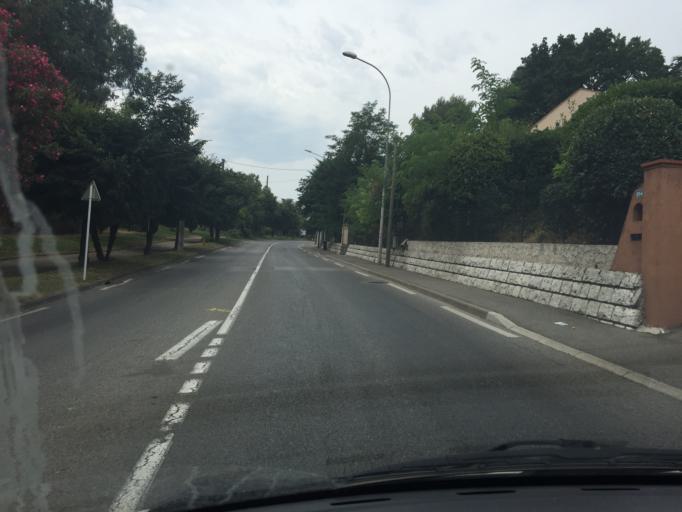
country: FR
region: Provence-Alpes-Cote d'Azur
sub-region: Departement des Alpes-Maritimes
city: Biot
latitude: 43.5943
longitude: 7.0973
